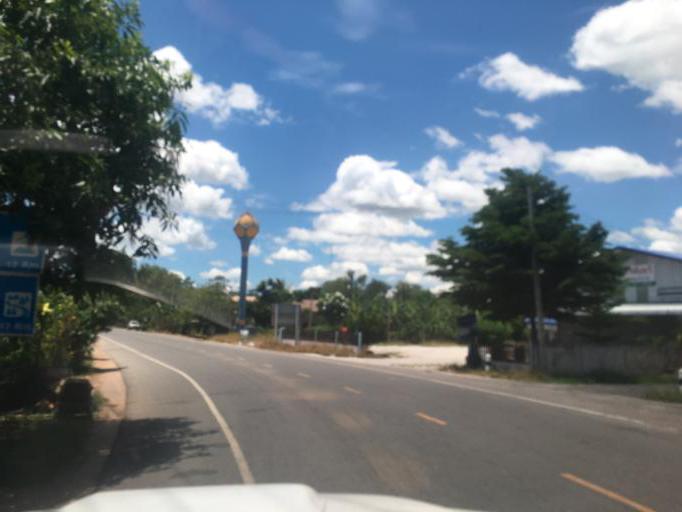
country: TH
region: Changwat Udon Thani
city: Nong Saeng
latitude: 17.2263
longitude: 102.7400
